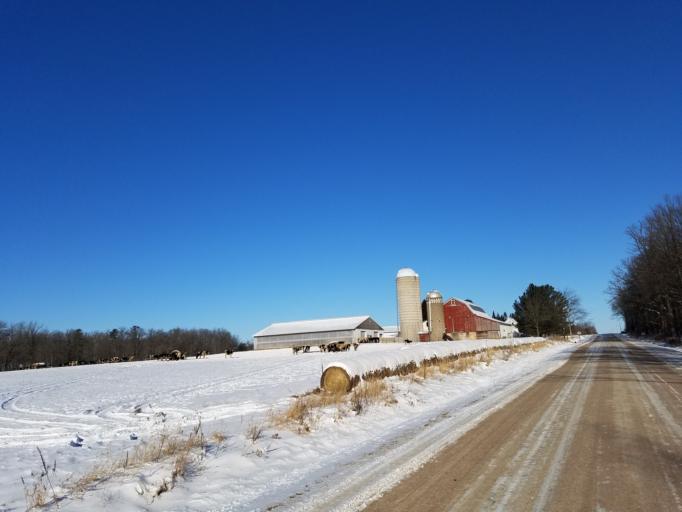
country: US
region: Wisconsin
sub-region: Clark County
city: Loyal
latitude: 44.6156
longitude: -90.3970
